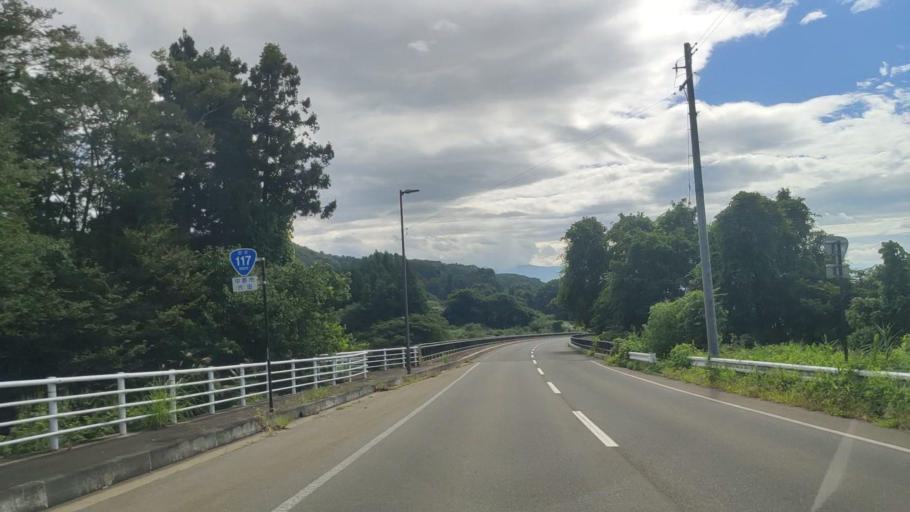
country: JP
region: Nagano
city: Nakano
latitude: 36.7915
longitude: 138.3168
